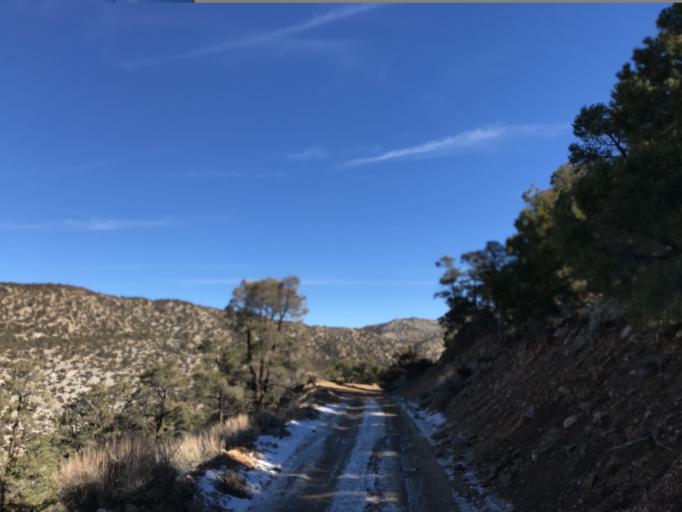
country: US
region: California
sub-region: San Bernardino County
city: Big Bear City
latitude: 34.2556
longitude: -116.7216
